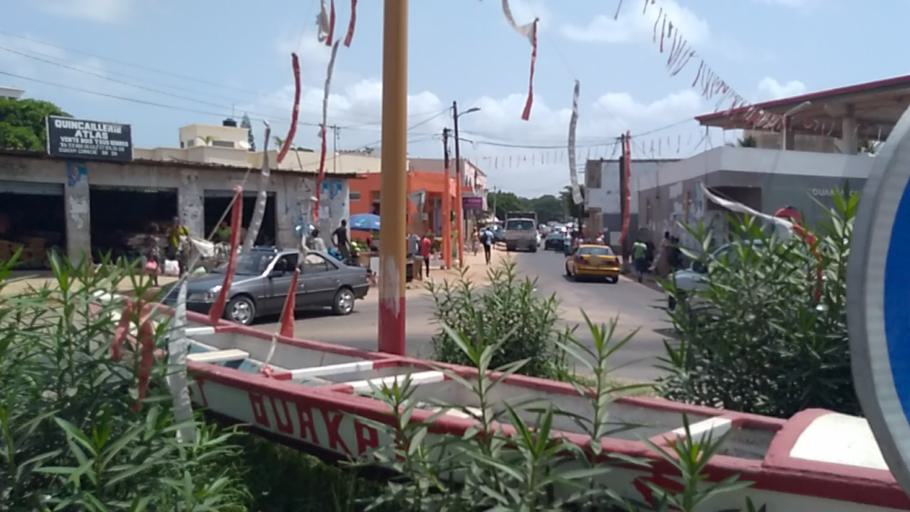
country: SN
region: Dakar
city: Mermoz Boabab
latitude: 14.7184
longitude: -17.4880
